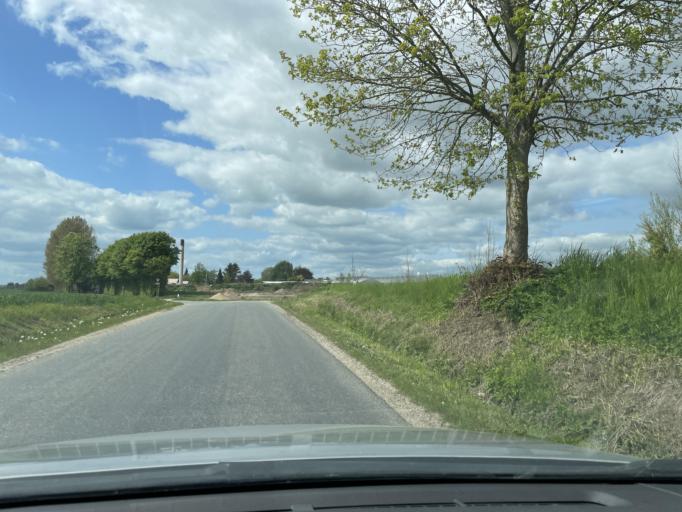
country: DK
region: Central Jutland
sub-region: Skanderborg Kommune
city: Skanderborg
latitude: 55.9277
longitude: 9.9513
